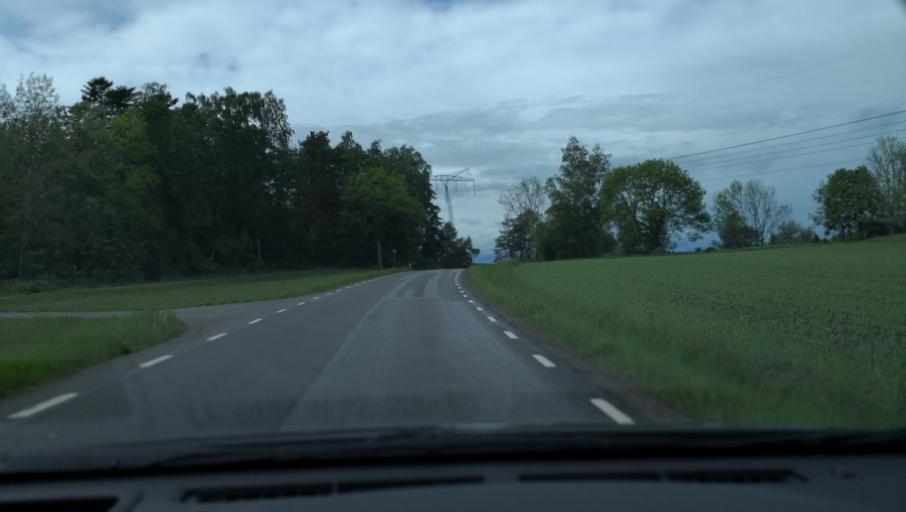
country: SE
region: Uppsala
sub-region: Enkopings Kommun
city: Orsundsbro
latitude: 59.6935
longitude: 17.3724
